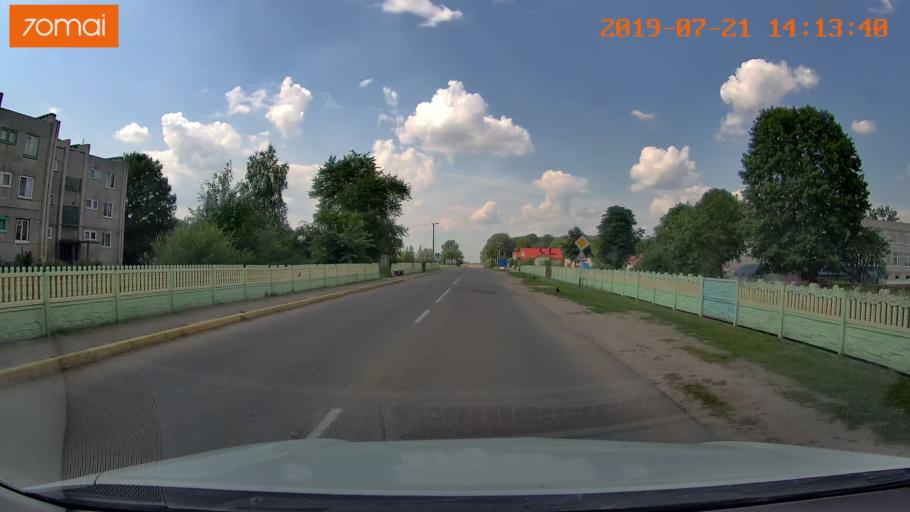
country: BY
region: Grodnenskaya
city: Karelichy
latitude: 53.6513
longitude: 26.1713
